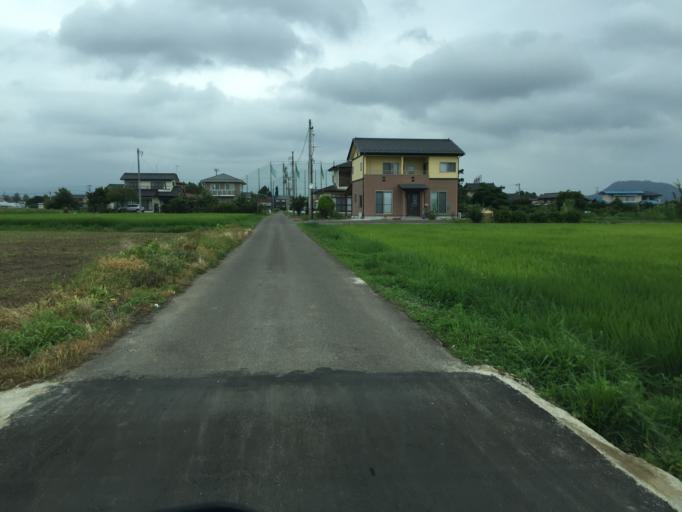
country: JP
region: Fukushima
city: Fukushima-shi
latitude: 37.7367
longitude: 140.4334
